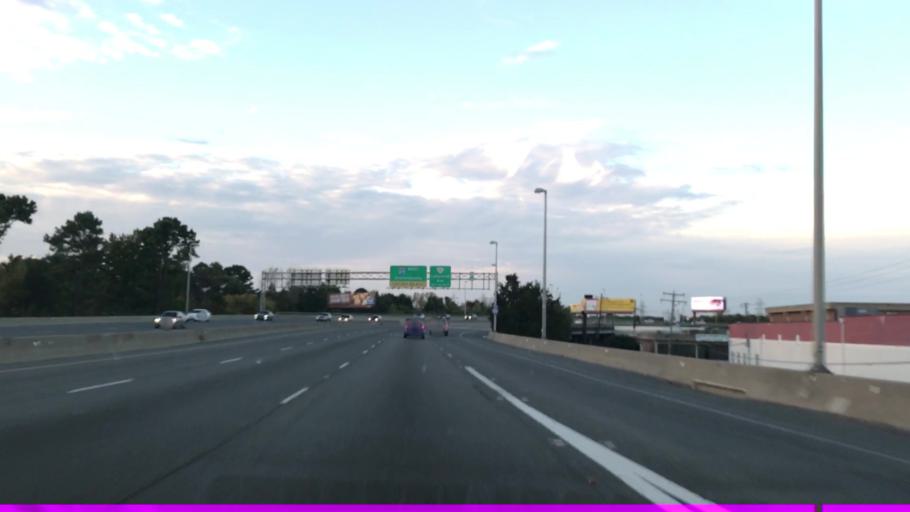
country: US
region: Virginia
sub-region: City of Richmond
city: Richmond
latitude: 37.5748
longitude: -77.4769
